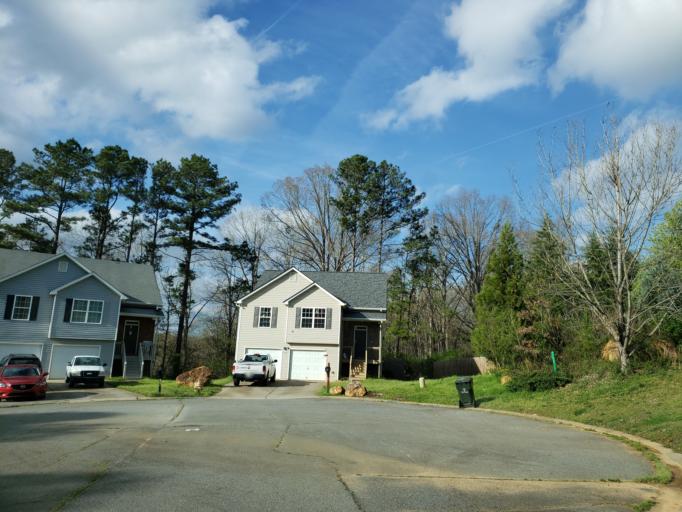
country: US
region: Georgia
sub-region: Bartow County
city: Emerson
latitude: 34.1181
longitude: -84.7586
